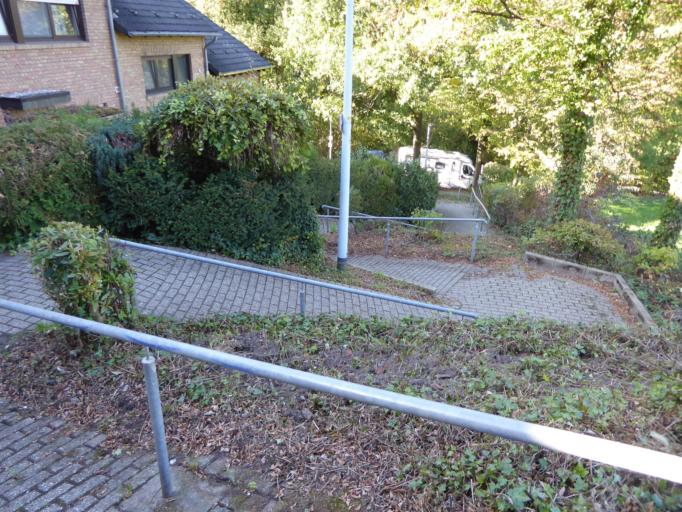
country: DE
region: North Rhine-Westphalia
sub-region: Regierungsbezirk Dusseldorf
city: Heiligenhaus
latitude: 51.3268
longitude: 6.9877
